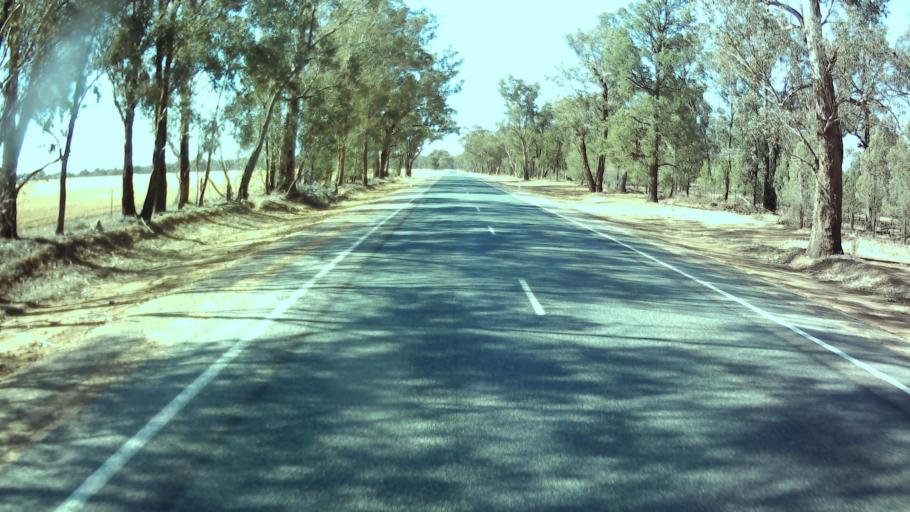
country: AU
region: New South Wales
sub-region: Weddin
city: Grenfell
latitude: -33.7389
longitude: 148.0887
